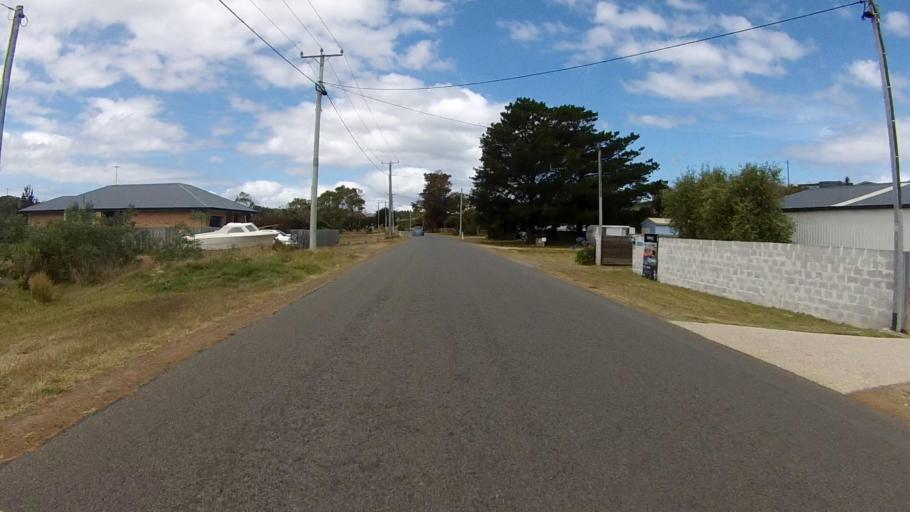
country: AU
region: Tasmania
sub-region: Sorell
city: Sorell
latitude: -42.8703
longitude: 147.6327
